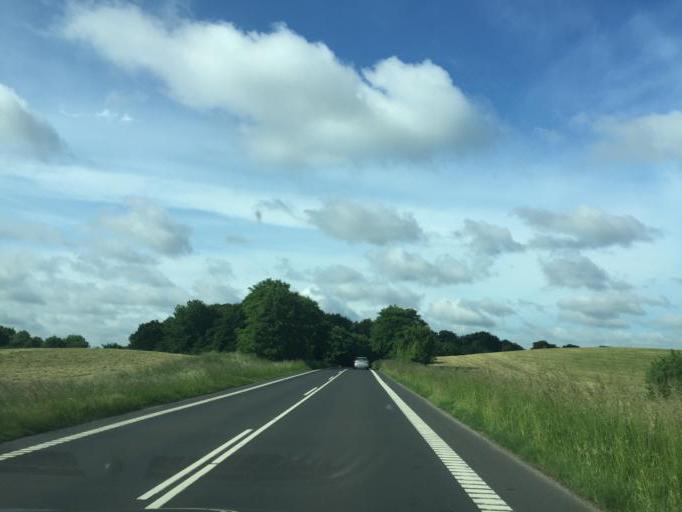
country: DK
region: South Denmark
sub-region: Kolding Kommune
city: Sonder Bjert
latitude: 55.5219
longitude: 9.5448
